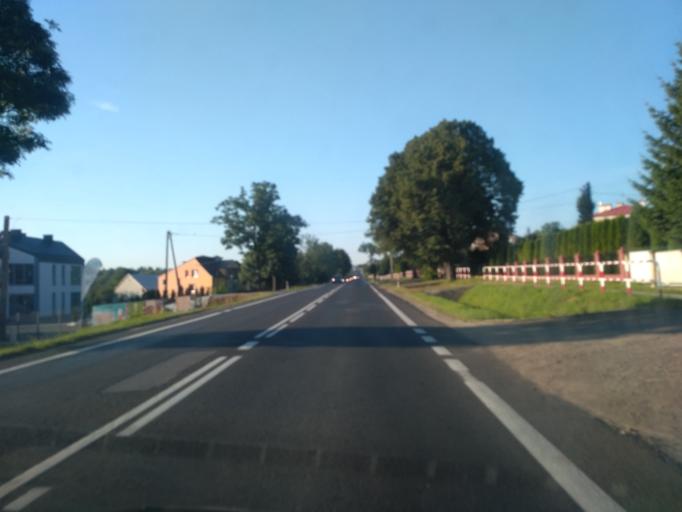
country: PL
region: Subcarpathian Voivodeship
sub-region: Powiat krosnienski
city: Miejsce Piastowe
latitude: 49.6417
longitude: 21.7848
